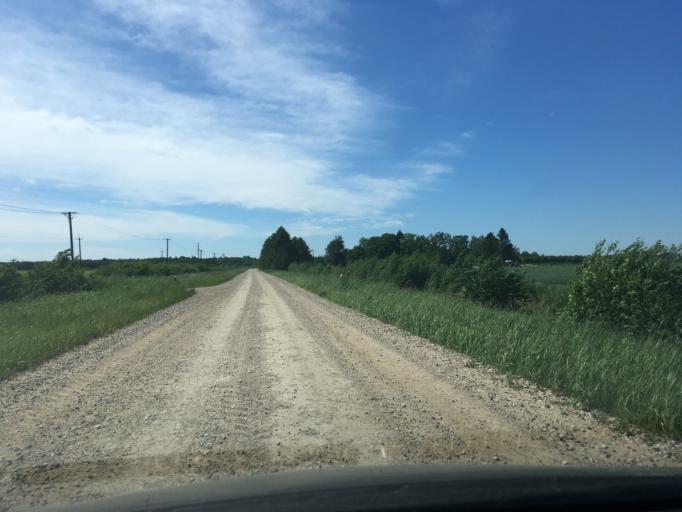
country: EE
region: Paernumaa
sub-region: Audru vald
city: Audru
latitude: 58.4663
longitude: 24.3948
